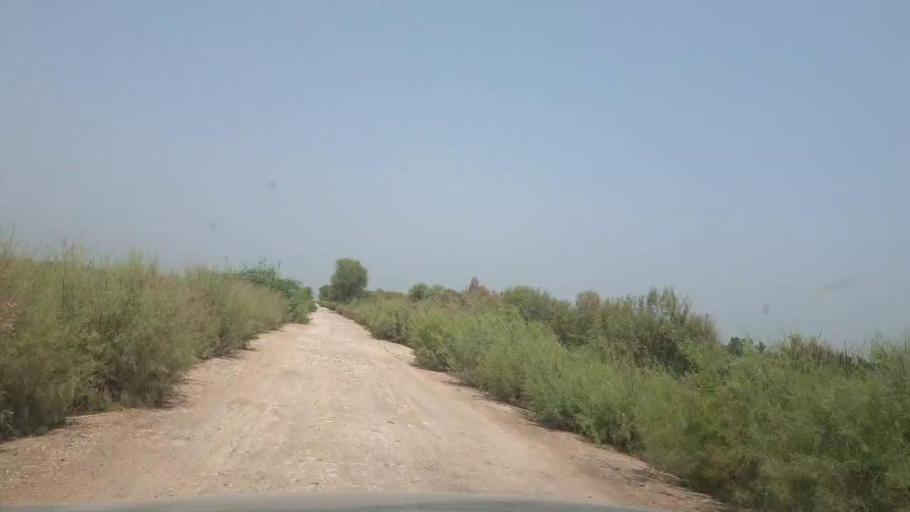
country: PK
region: Sindh
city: Lakhi
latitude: 27.8346
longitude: 68.6243
